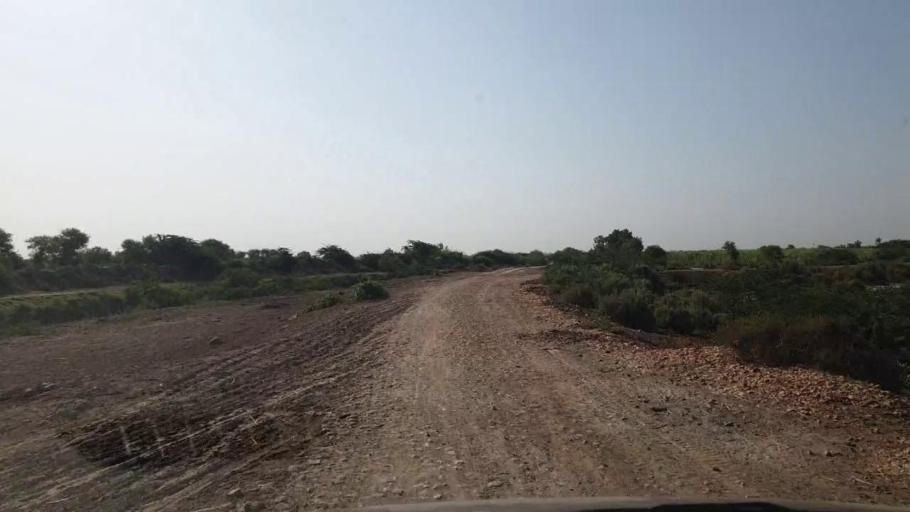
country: PK
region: Sindh
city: Kadhan
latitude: 24.6196
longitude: 69.0733
